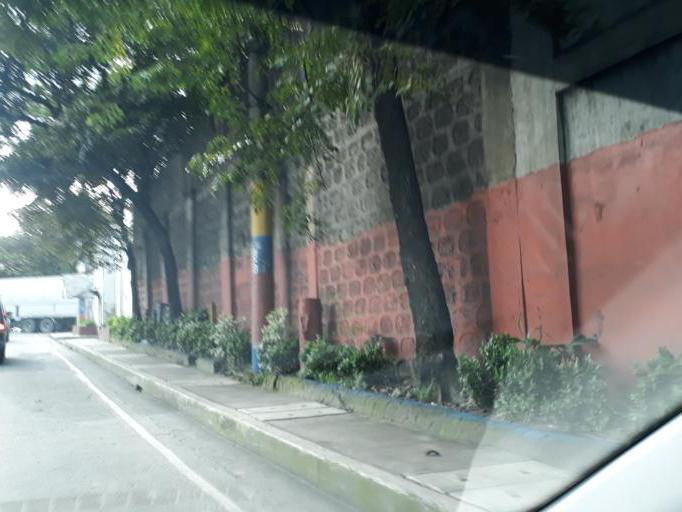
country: PH
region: Metro Manila
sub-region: Caloocan City
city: Niugan
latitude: 14.6673
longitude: 120.9787
